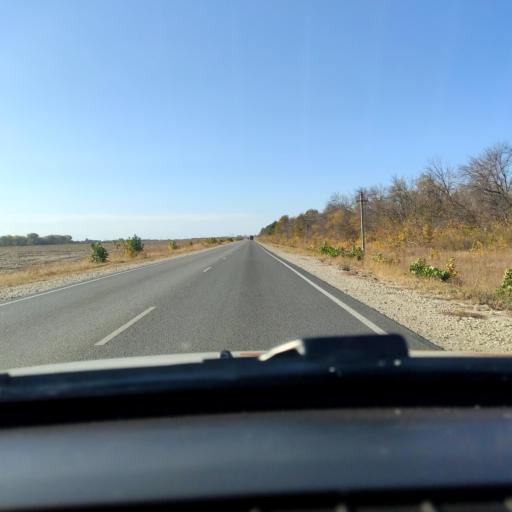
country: RU
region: Voronezj
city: Semiluki
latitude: 51.7299
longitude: 38.9770
